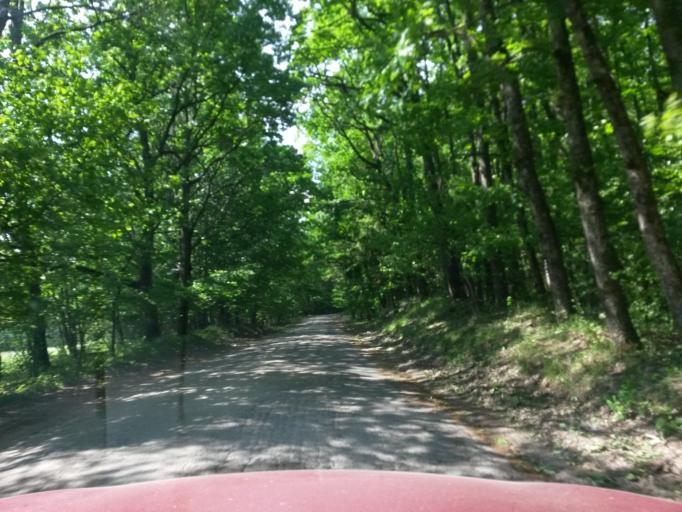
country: SK
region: Kosicky
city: Moldava nad Bodvou
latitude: 48.7152
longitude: 21.0264
